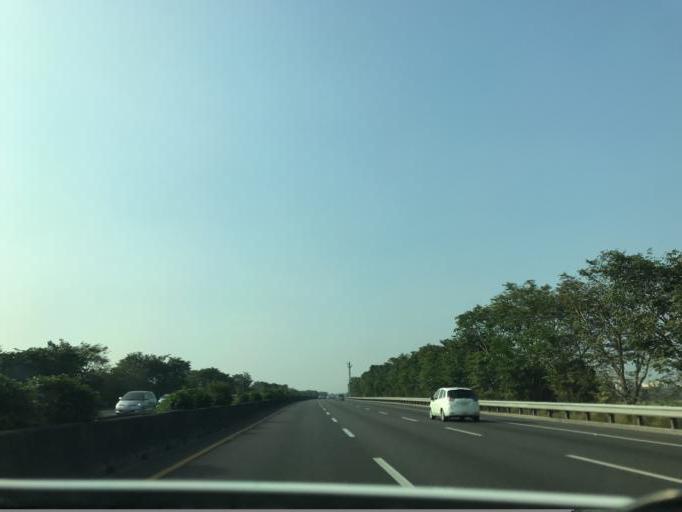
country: TW
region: Taiwan
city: Xinying
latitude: 23.3730
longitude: 120.3506
